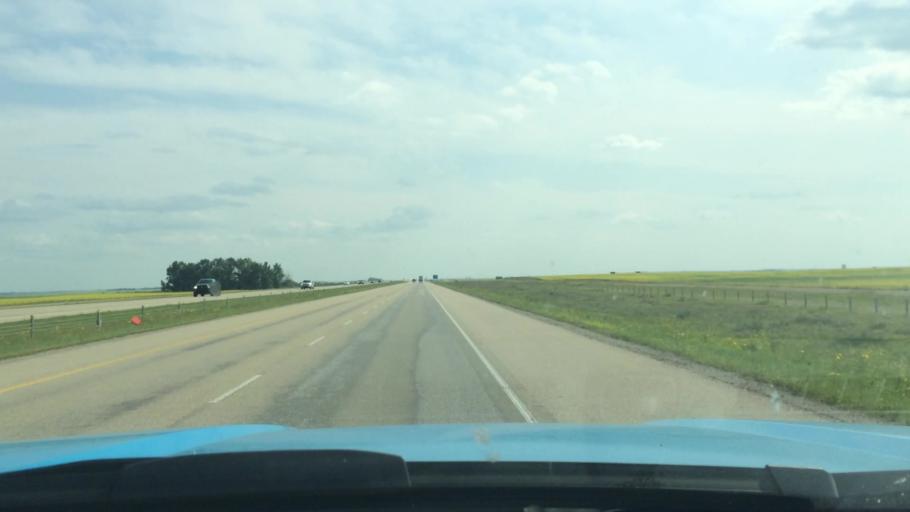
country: CA
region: Alberta
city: Carstairs
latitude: 51.5887
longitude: -114.0253
